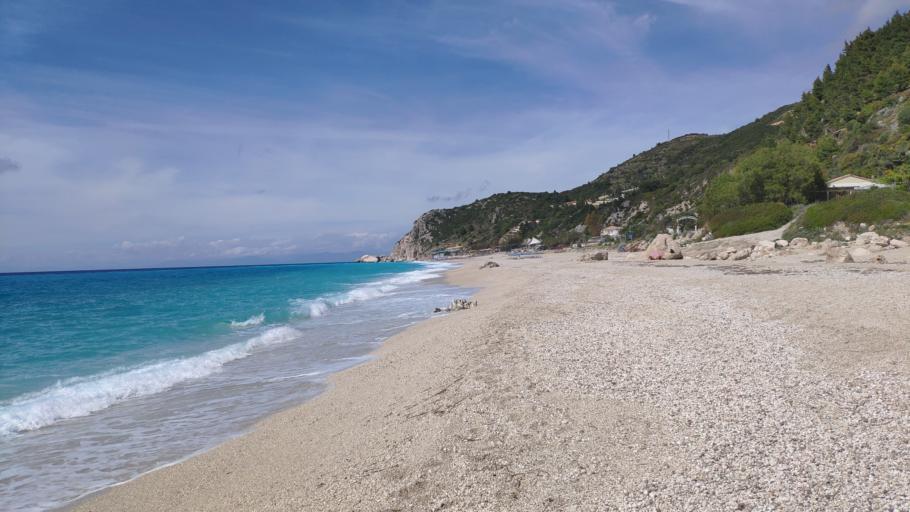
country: GR
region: Ionian Islands
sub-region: Lefkada
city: Lefkada
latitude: 38.7725
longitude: 20.5982
